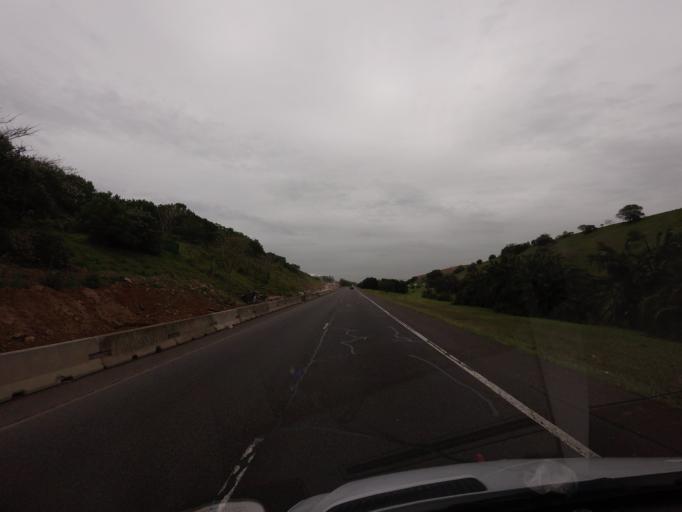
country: ZA
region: KwaZulu-Natal
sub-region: eThekwini Metropolitan Municipality
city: Durban
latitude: -29.7063
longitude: 31.0683
